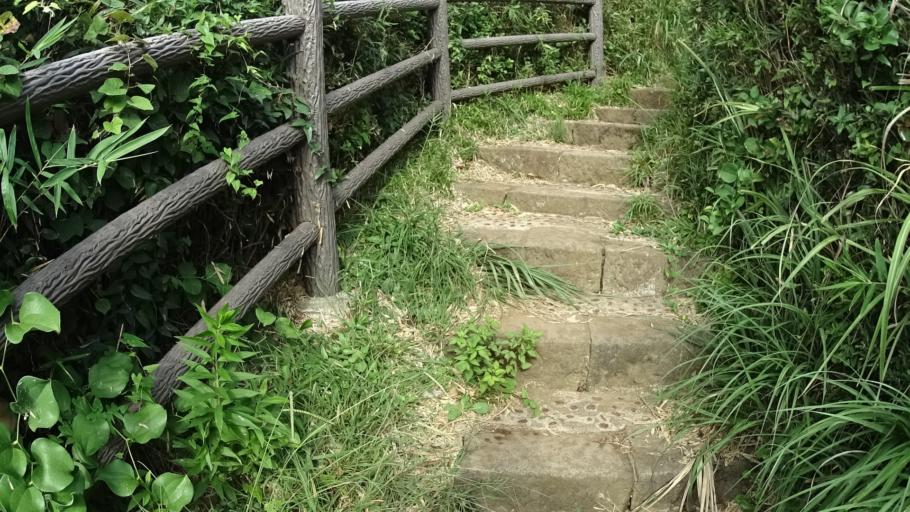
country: JP
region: Kanagawa
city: Miura
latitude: 35.1306
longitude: 139.6257
